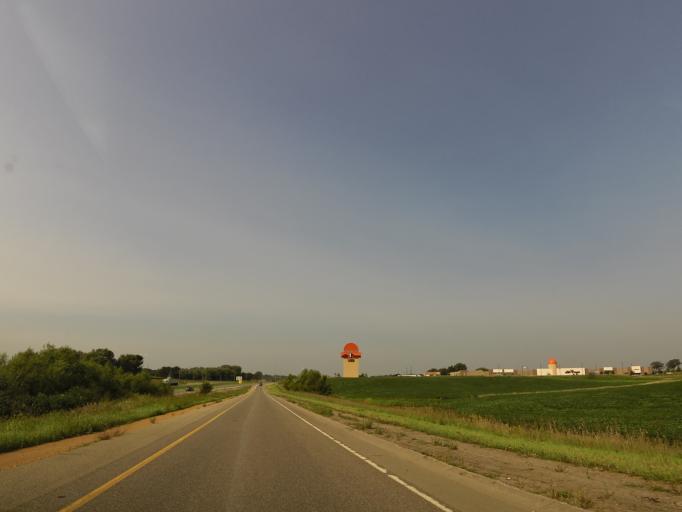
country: US
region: Minnesota
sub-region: Carver County
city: Carver
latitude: 44.7774
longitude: -93.6439
